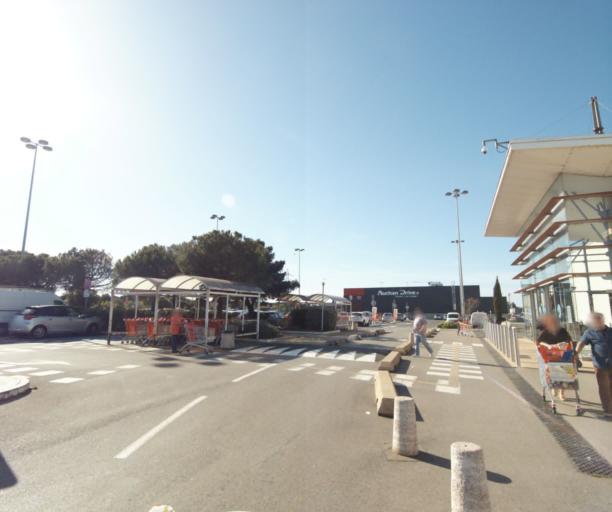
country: FR
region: Languedoc-Roussillon
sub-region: Departement de l'Herault
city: Perols
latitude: 43.5713
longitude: 3.9403
